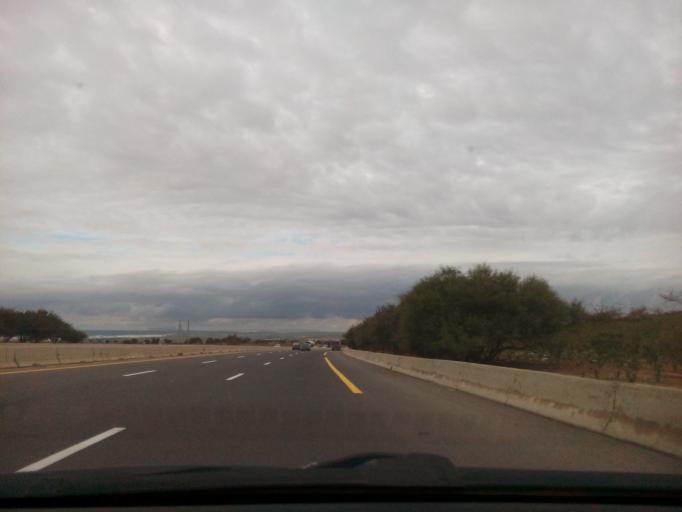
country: DZ
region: Sidi Bel Abbes
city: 'Ain el Berd
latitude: 35.4865
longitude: -0.3863
